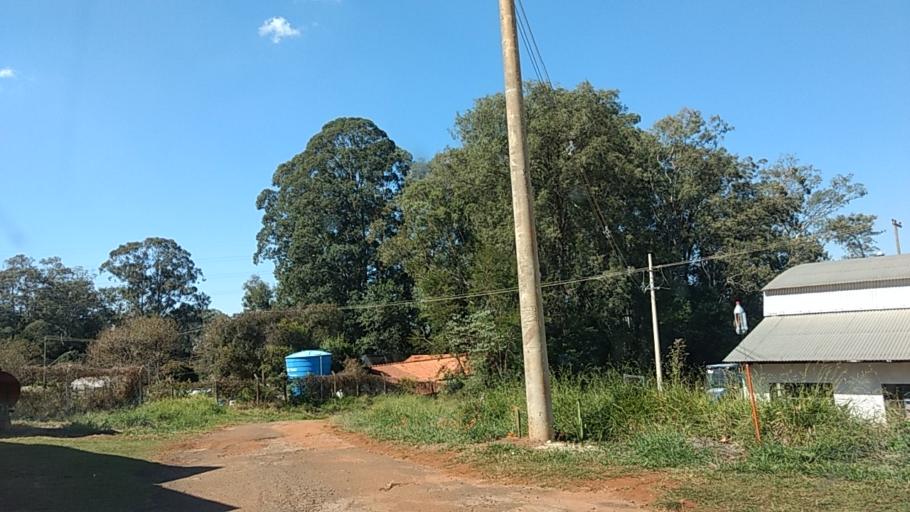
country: BR
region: Sao Paulo
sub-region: Botucatu
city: Botucatu
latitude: -22.8568
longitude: -48.4346
